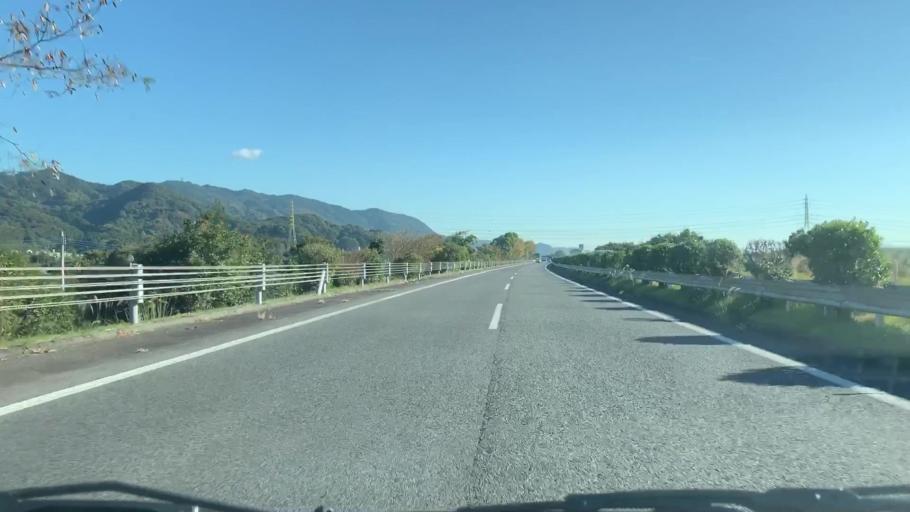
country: JP
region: Saga Prefecture
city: Saga-shi
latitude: 33.3167
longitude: 130.2618
